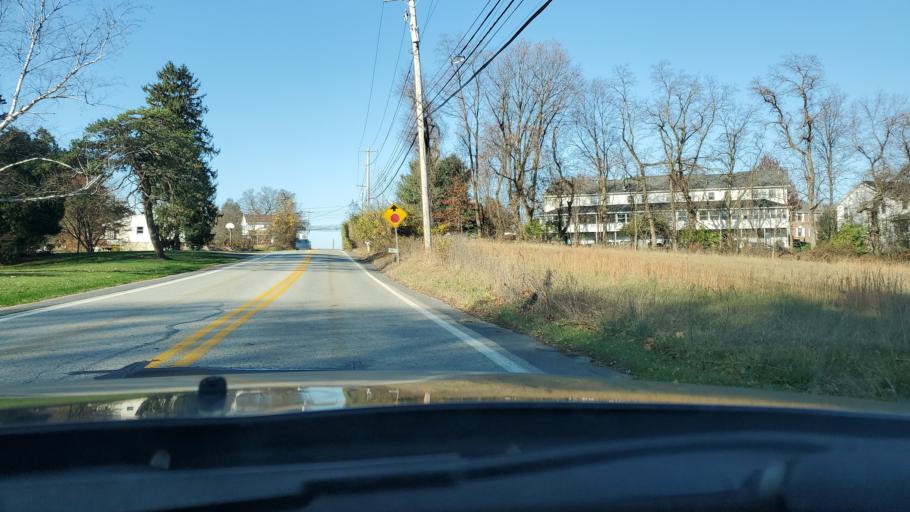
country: US
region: Pennsylvania
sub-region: Cumberland County
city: Mechanicsburg
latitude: 40.1631
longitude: -76.9951
